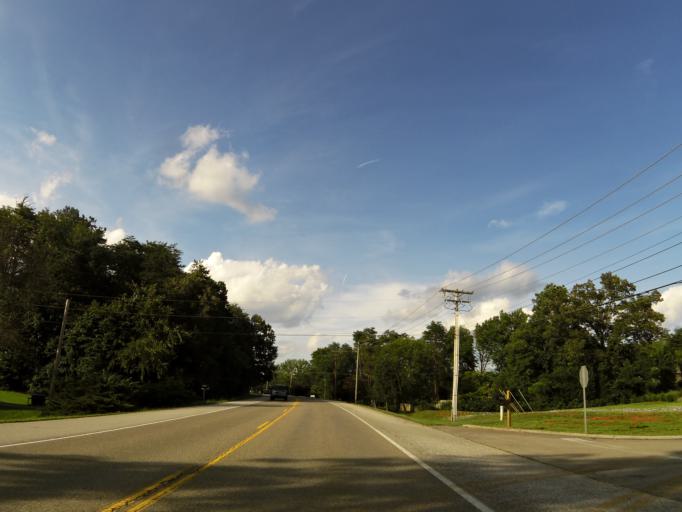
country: US
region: Tennessee
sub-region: Blount County
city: Louisville
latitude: 35.8250
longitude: -84.0198
